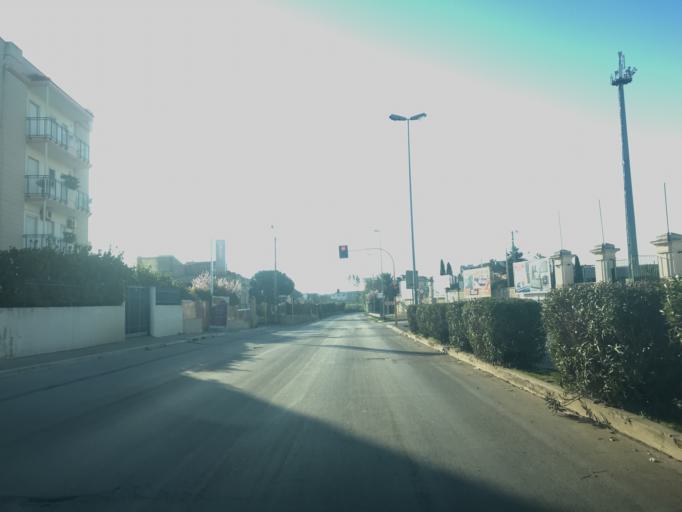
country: IT
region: Apulia
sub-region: Provincia di Bari
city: Corato
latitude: 41.1429
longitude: 16.4137
